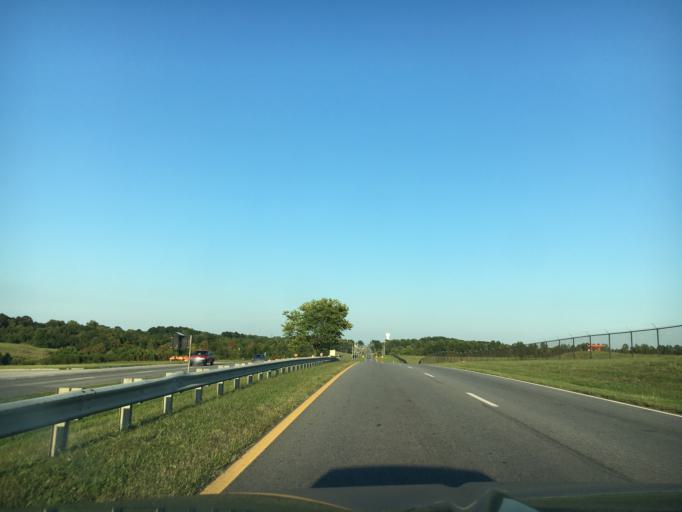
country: US
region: Virginia
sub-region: City of Danville
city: Danville
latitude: 36.5809
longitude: -79.3369
